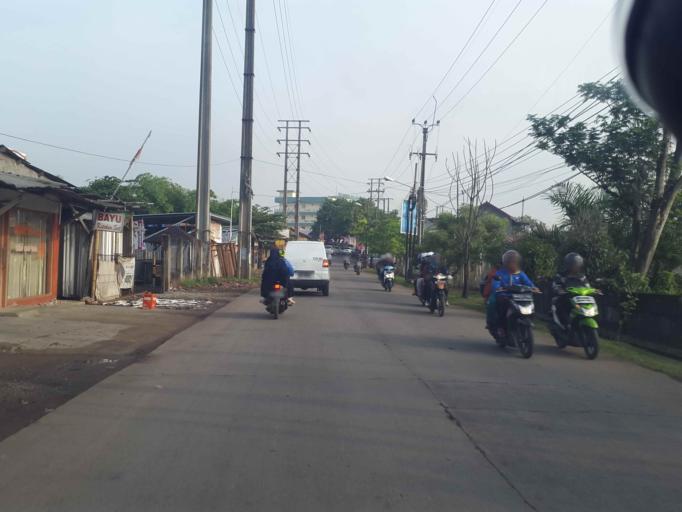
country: ID
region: West Java
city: Bekasi
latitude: -6.2940
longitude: 107.0313
